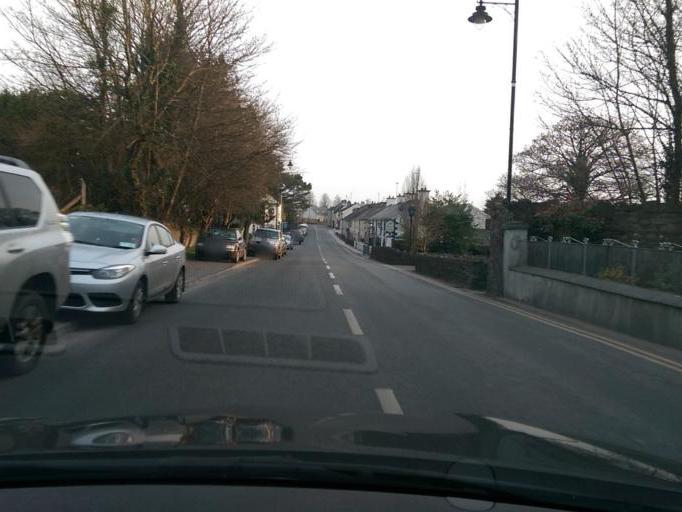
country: IE
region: Leinster
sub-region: An Iarmhi
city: Athlone
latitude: 53.4717
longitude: -7.8639
